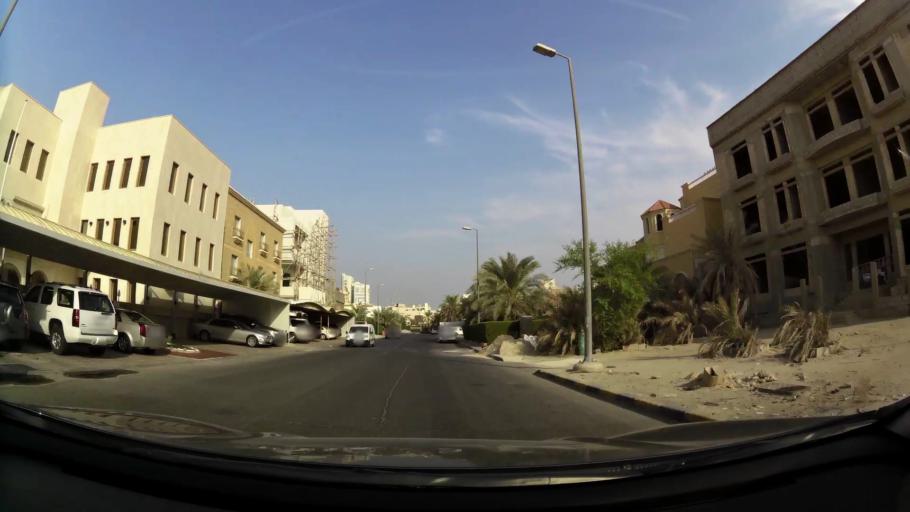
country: KW
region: Muhafazat Hawalli
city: Hawalli
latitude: 29.3236
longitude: 48.0065
